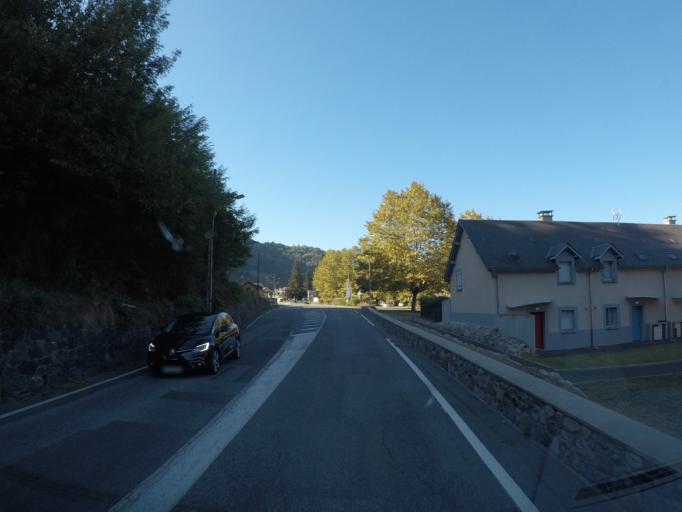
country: FR
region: Midi-Pyrenees
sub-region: Departement des Hautes-Pyrenees
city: Pierrefitte-Nestalas
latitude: 42.9541
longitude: -0.0708
